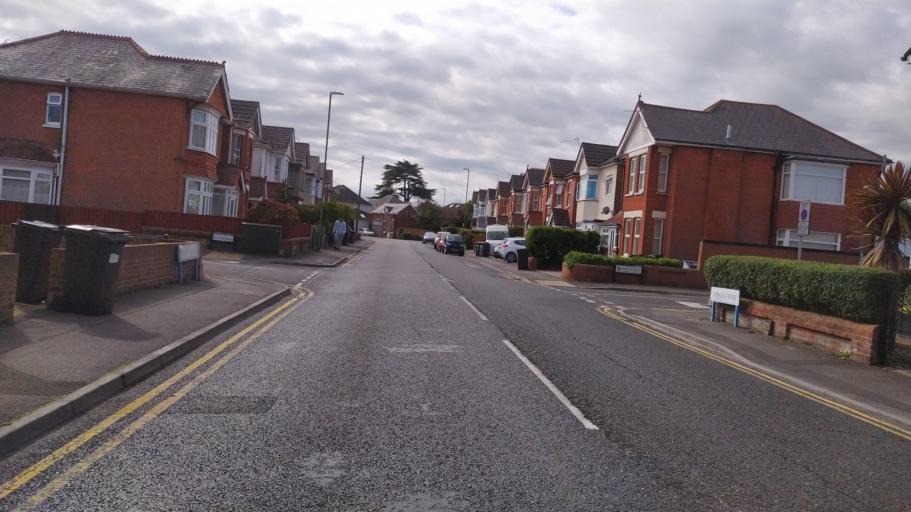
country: GB
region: England
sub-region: Bournemouth
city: Bournemouth
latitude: 50.7454
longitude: -1.8847
